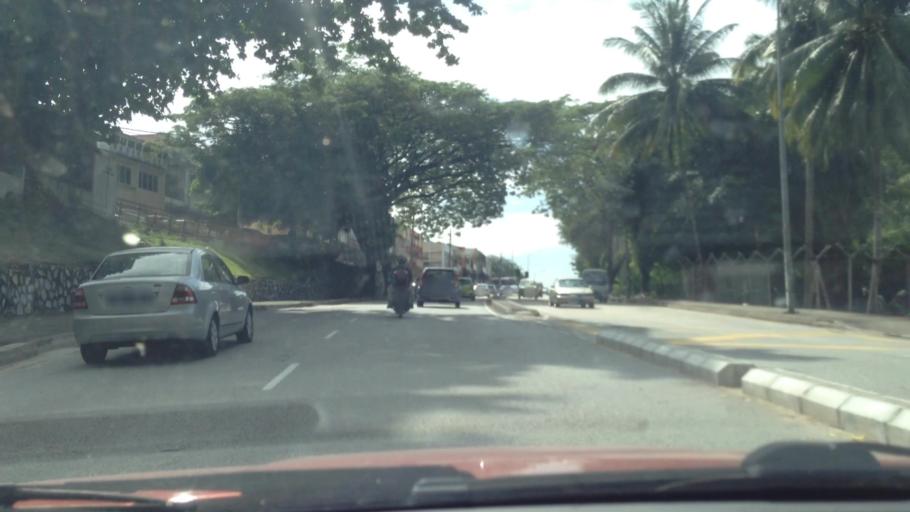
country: MY
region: Kuala Lumpur
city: Kuala Lumpur
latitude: 3.0907
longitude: 101.6776
